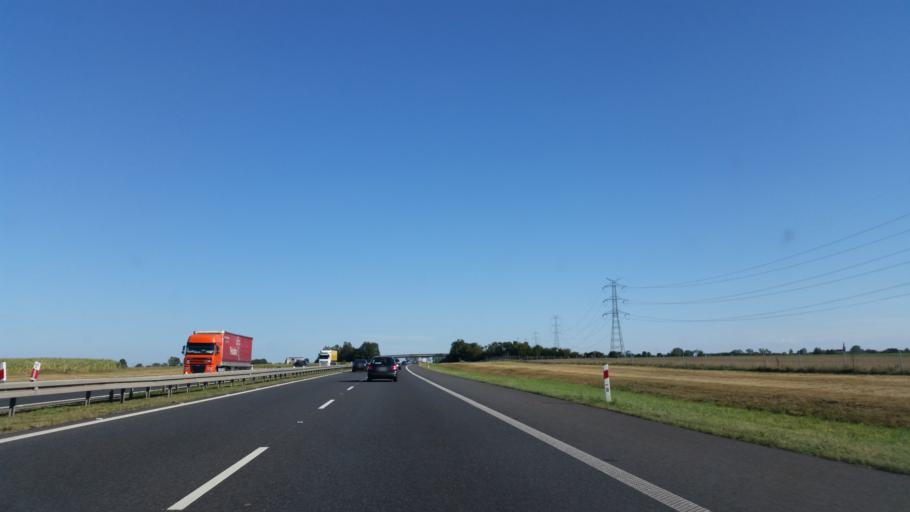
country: PL
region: Lower Silesian Voivodeship
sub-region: Powiat strzelinski
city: Wiazow
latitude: 50.8194
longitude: 17.3040
